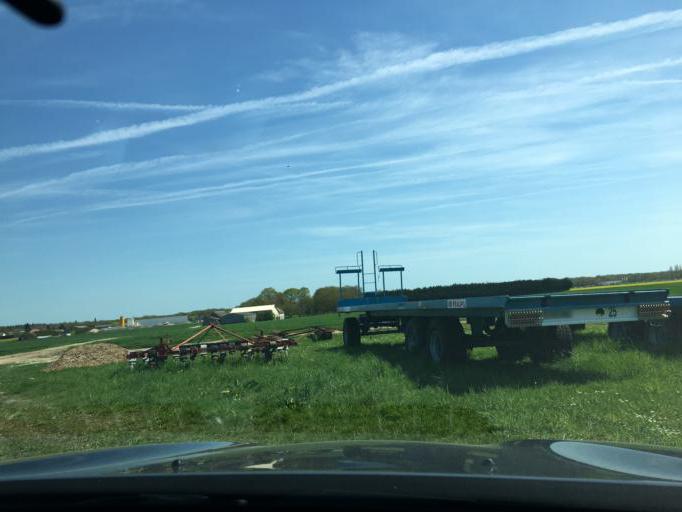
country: FR
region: Centre
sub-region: Departement du Loiret
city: Saran
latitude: 47.9782
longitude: 1.8734
